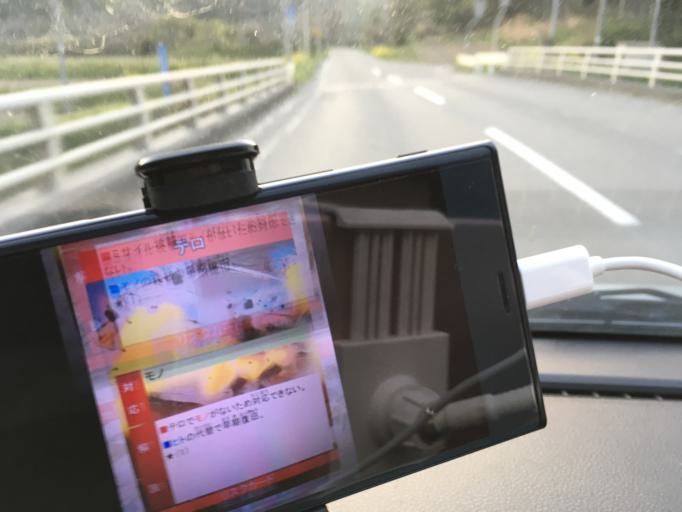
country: JP
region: Iwate
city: Ichinoseki
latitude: 38.9413
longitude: 141.2121
